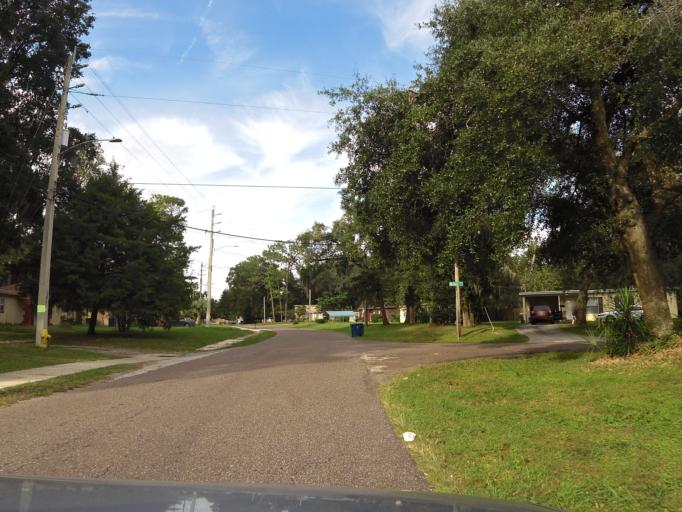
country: US
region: Florida
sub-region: Duval County
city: Jacksonville
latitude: 30.4280
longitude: -81.6784
